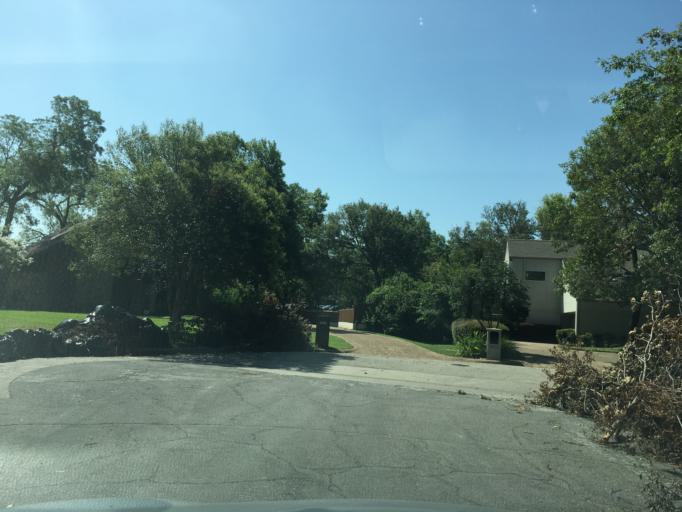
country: US
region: Texas
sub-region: Dallas County
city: Richardson
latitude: 32.9076
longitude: -96.7734
